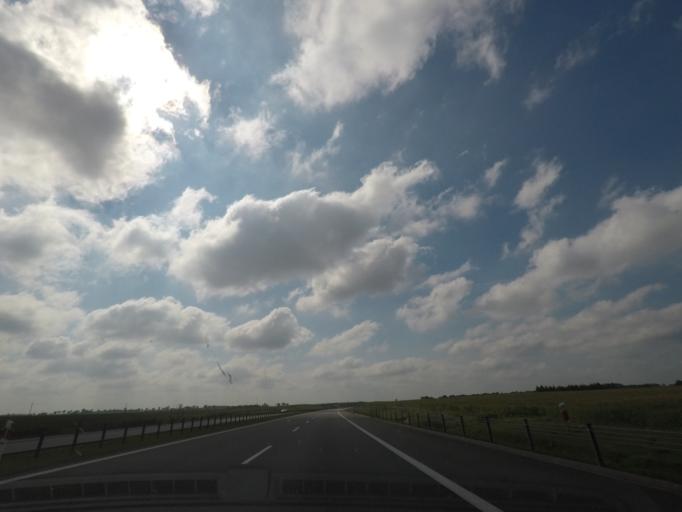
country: PL
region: Kujawsko-Pomorskie
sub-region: Powiat wabrzeski
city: Pluznica
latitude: 53.2173
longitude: 18.7354
